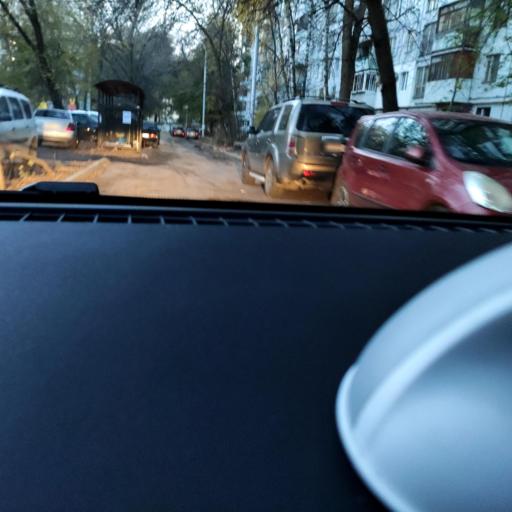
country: RU
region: Samara
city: Petra-Dubrava
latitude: 53.2464
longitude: 50.2654
